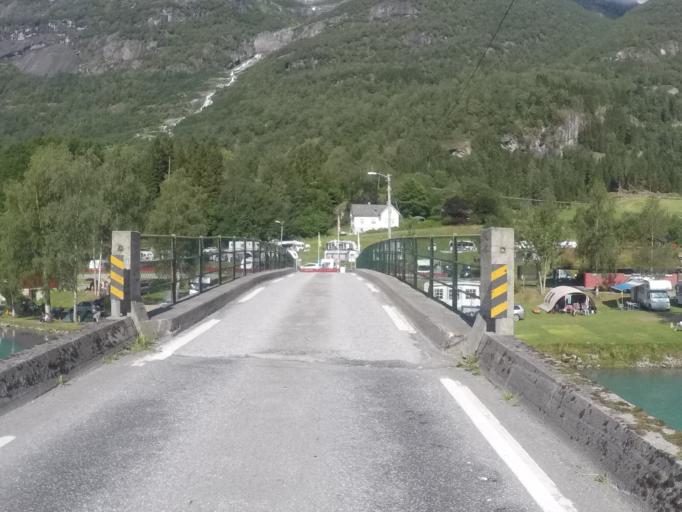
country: NO
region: Sogn og Fjordane
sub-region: Stryn
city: Stryn
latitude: 61.7578
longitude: 6.8129
